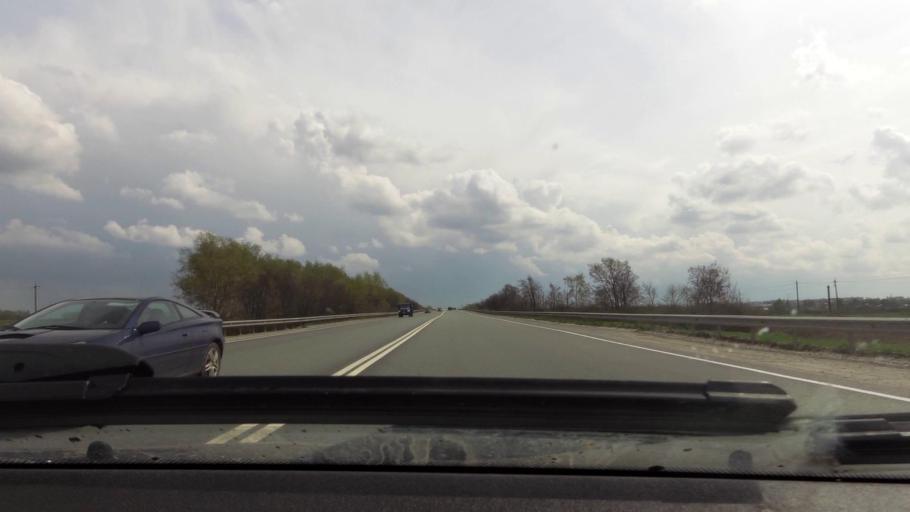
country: RU
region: Rjazan
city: Bagramovo
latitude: 54.7400
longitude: 39.4451
